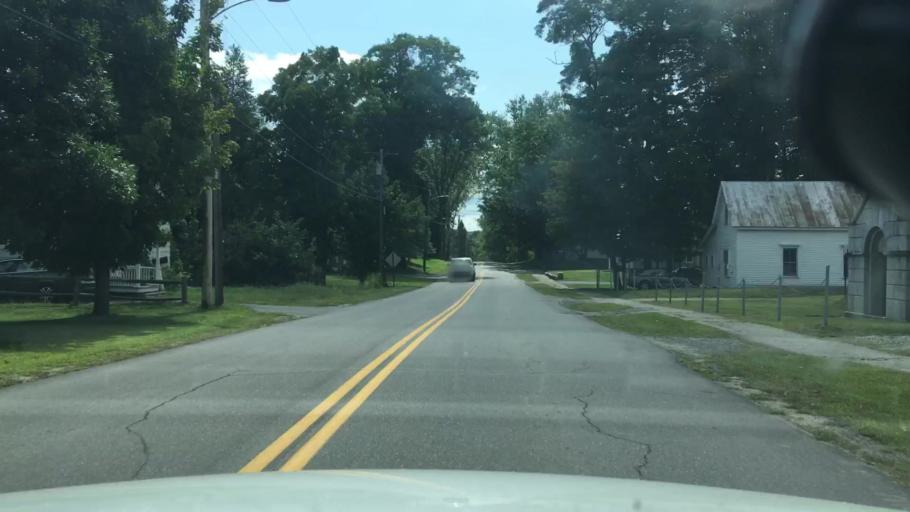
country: US
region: Maine
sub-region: Somerset County
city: Skowhegan
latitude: 44.7560
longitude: -69.7170
